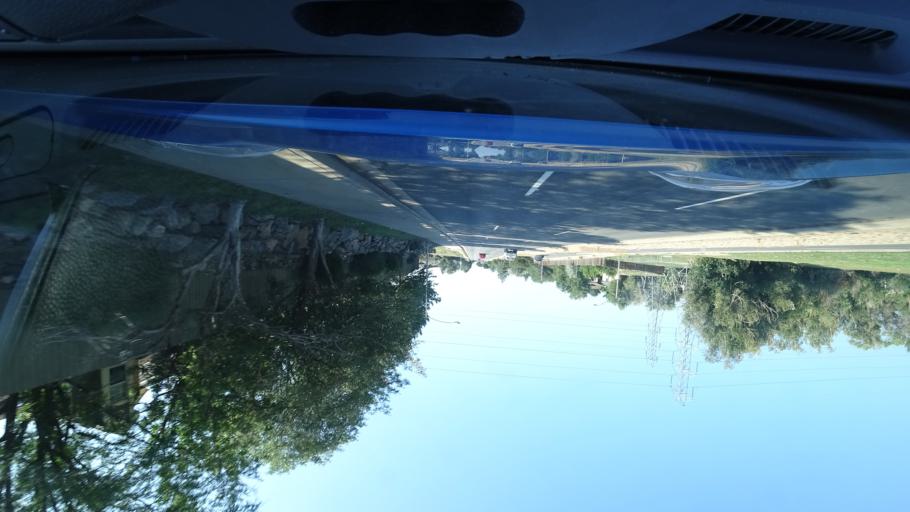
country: US
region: Colorado
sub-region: Adams County
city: Aurora
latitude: 39.6814
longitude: -104.8098
